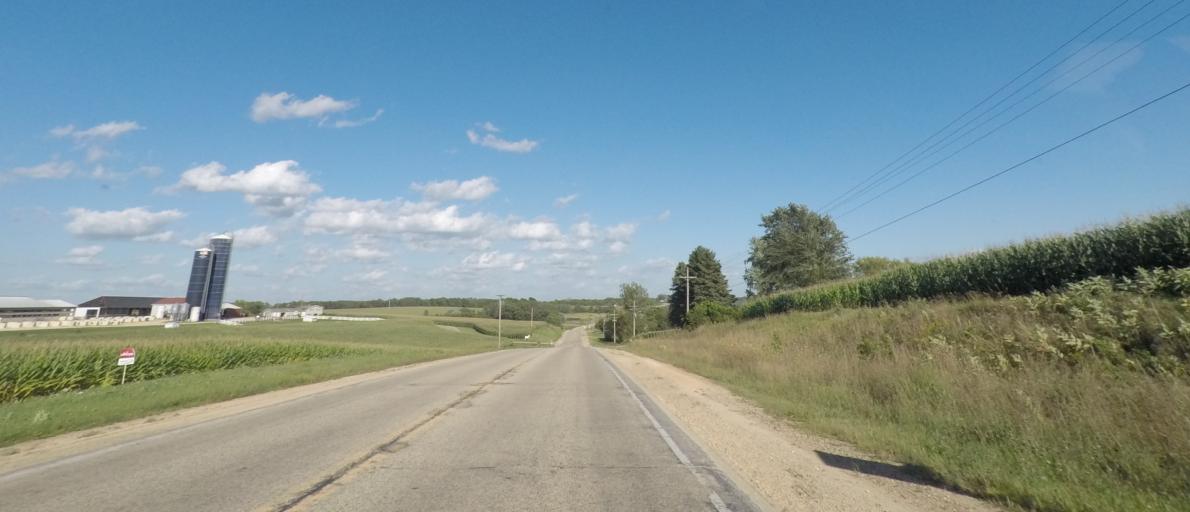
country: US
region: Wisconsin
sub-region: Iowa County
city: Dodgeville
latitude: 42.9816
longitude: -90.0868
